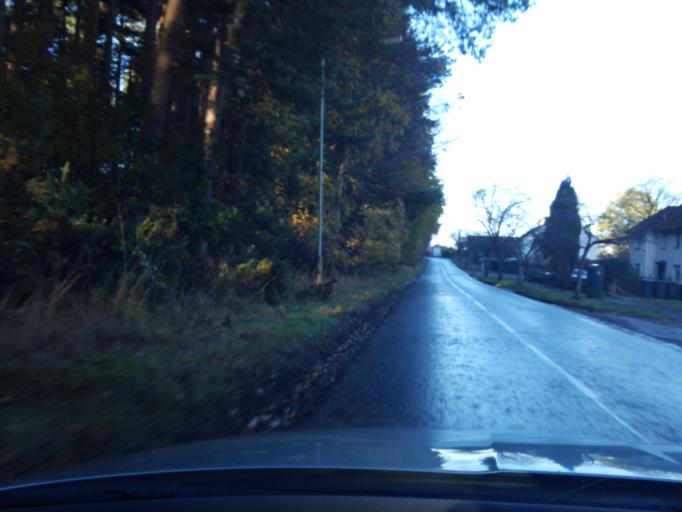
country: GB
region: Scotland
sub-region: Perth and Kinross
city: Scone
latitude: 56.4247
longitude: -3.4153
